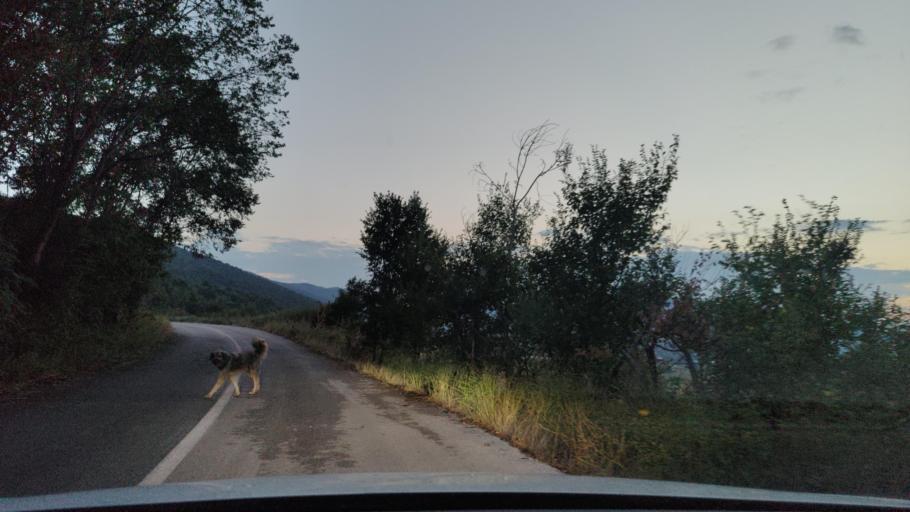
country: GR
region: Central Macedonia
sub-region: Nomos Serron
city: Chrysochorafa
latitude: 41.1784
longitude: 23.1244
